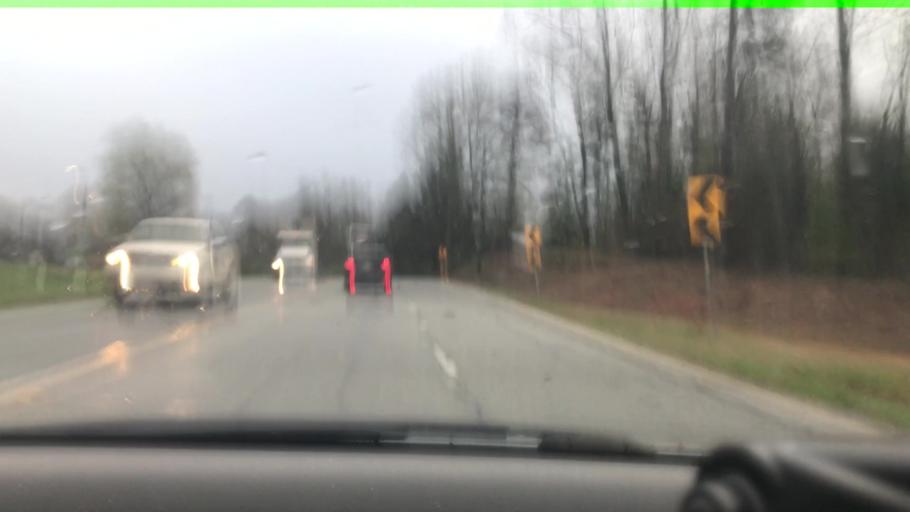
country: US
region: Georgia
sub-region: Oglethorpe County
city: Lexington
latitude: 33.8822
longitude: -83.1612
